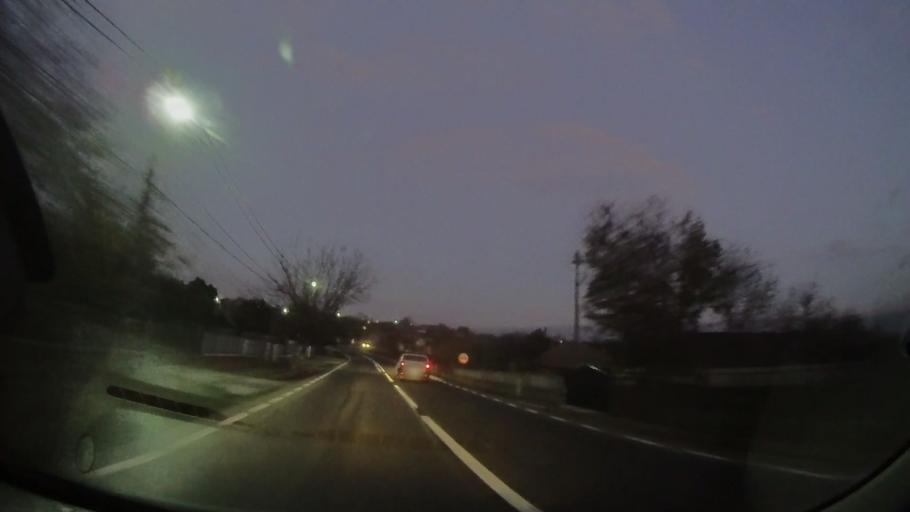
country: RO
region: Tulcea
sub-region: Comuna Frecatei
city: Cataloi
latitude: 45.0984
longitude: 28.7263
